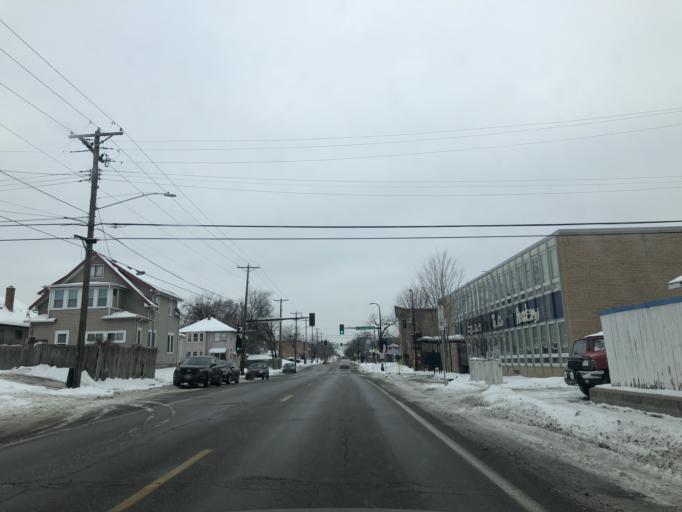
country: US
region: Minnesota
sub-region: Anoka County
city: Columbia Heights
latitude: 45.0240
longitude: -93.2935
